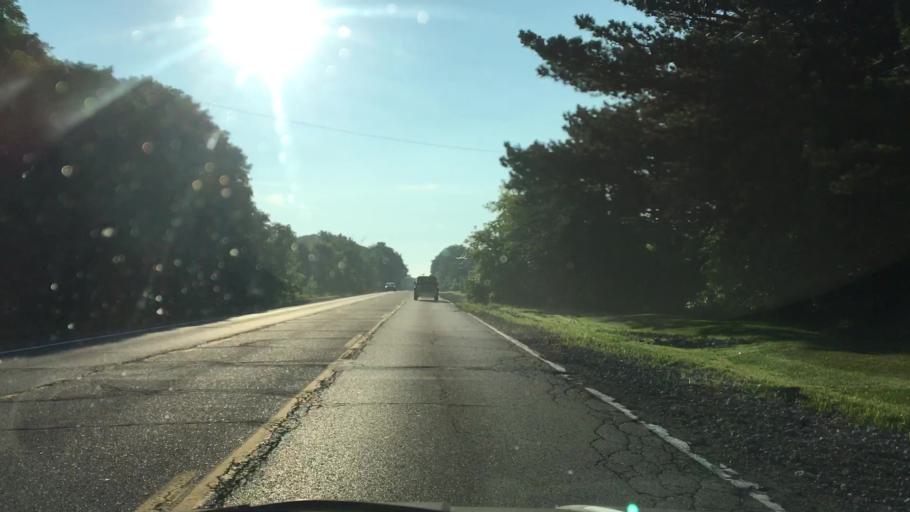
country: US
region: Michigan
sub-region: Oakland County
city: South Lyon
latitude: 42.5166
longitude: -83.6477
